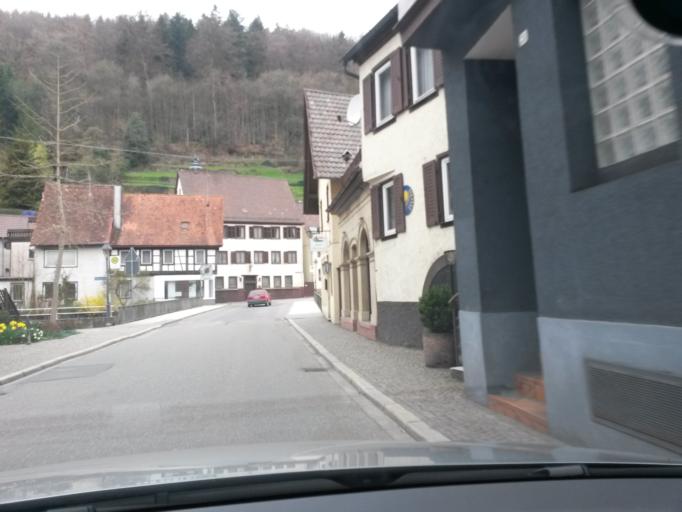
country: DE
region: Baden-Wuerttemberg
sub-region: Karlsruhe Region
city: Neuenburg
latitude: 48.8466
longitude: 8.5884
